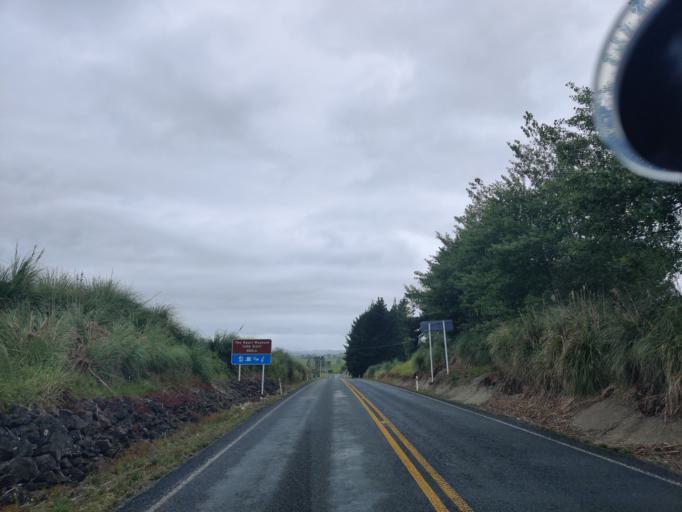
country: NZ
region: Northland
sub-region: Kaipara District
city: Dargaville
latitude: -36.1290
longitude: 174.1402
